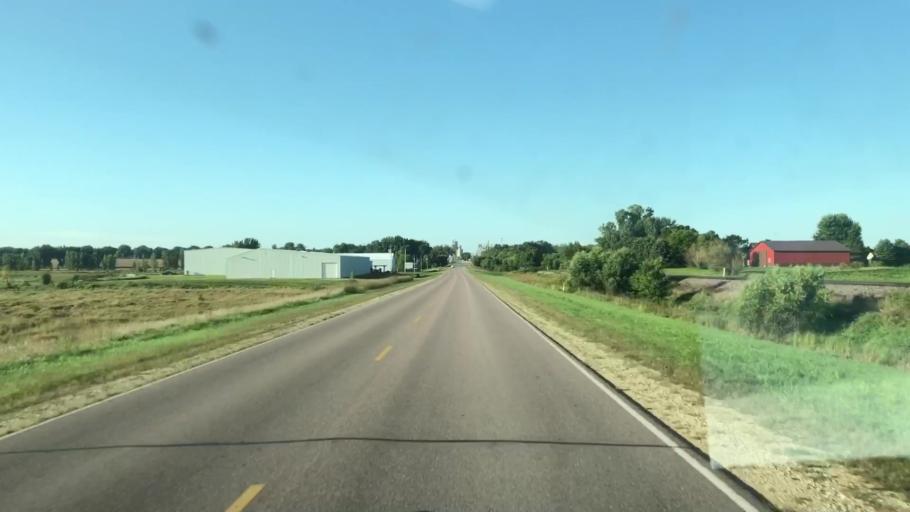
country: US
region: Iowa
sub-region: O'Brien County
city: Sheldon
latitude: 43.2017
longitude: -95.8460
